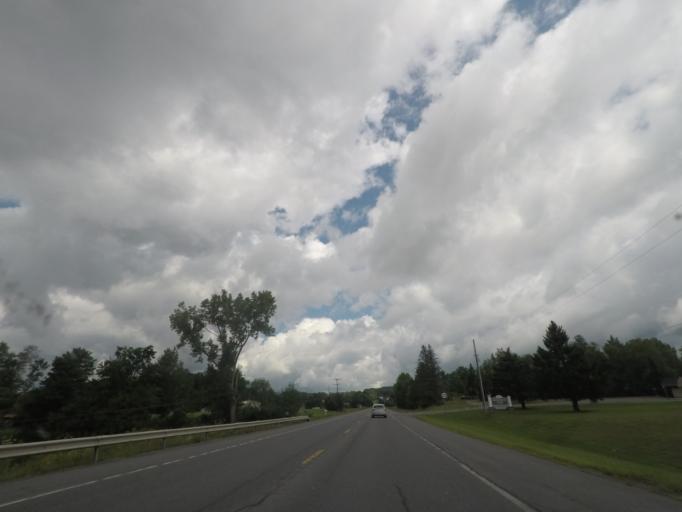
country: US
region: Massachusetts
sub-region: Berkshire County
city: Lanesborough
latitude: 42.5917
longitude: -73.3685
